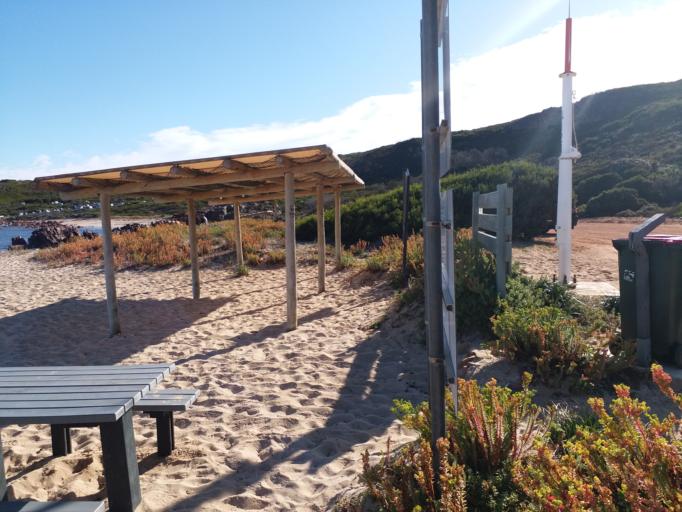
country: AU
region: Western Australia
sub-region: Augusta-Margaret River Shire
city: Margaret River
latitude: -33.8617
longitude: 114.9889
